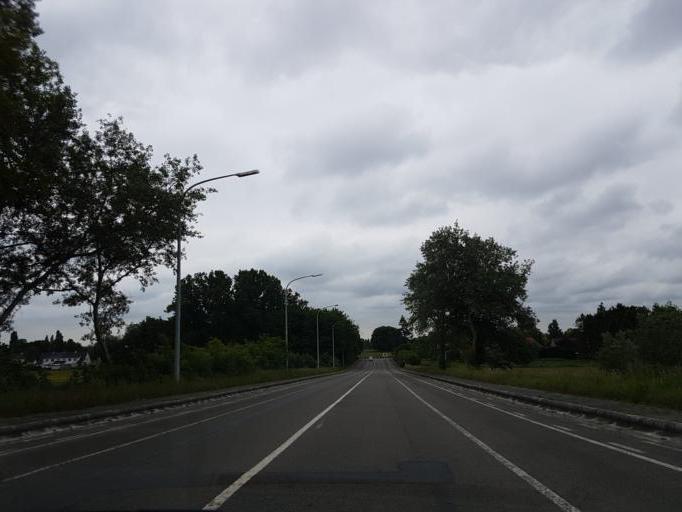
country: BE
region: Flanders
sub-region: Provincie Oost-Vlaanderen
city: Lovendegem
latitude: 51.0904
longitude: 3.6036
